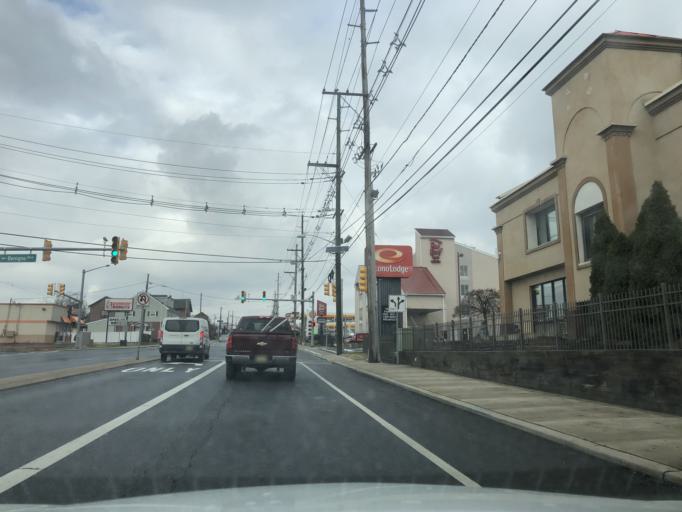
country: US
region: New Jersey
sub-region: Camden County
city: Runnemede
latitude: 39.8635
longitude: -75.0781
